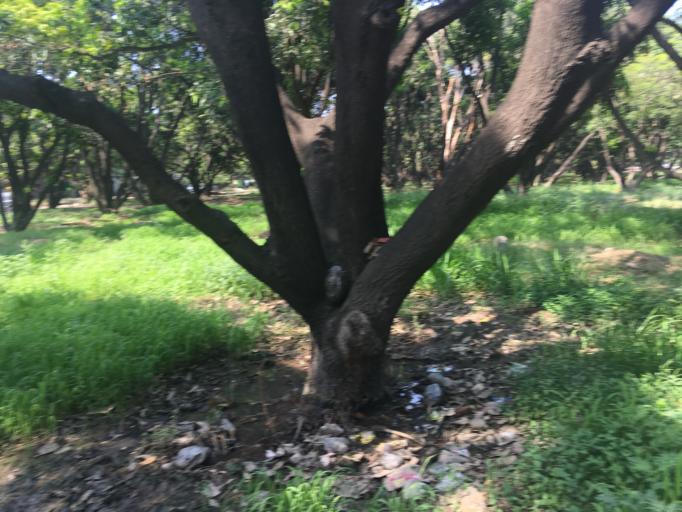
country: IN
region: Chandigarh
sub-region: Chandigarh
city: Chandigarh
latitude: 30.7075
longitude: 76.7952
